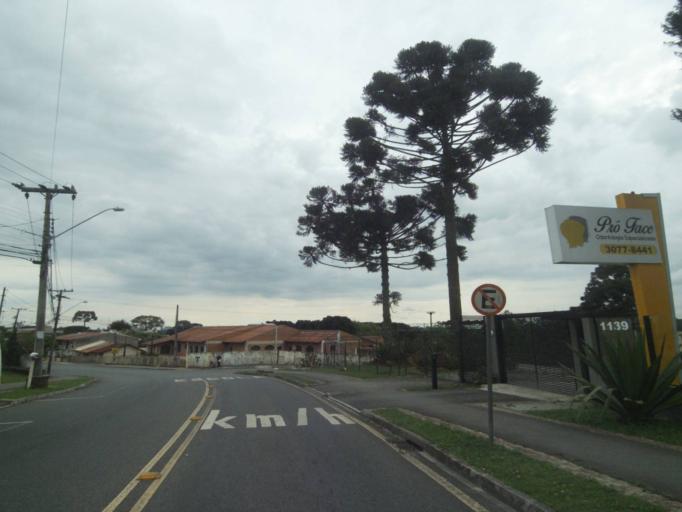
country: BR
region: Parana
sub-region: Curitiba
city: Curitiba
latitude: -25.3972
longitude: -49.2963
